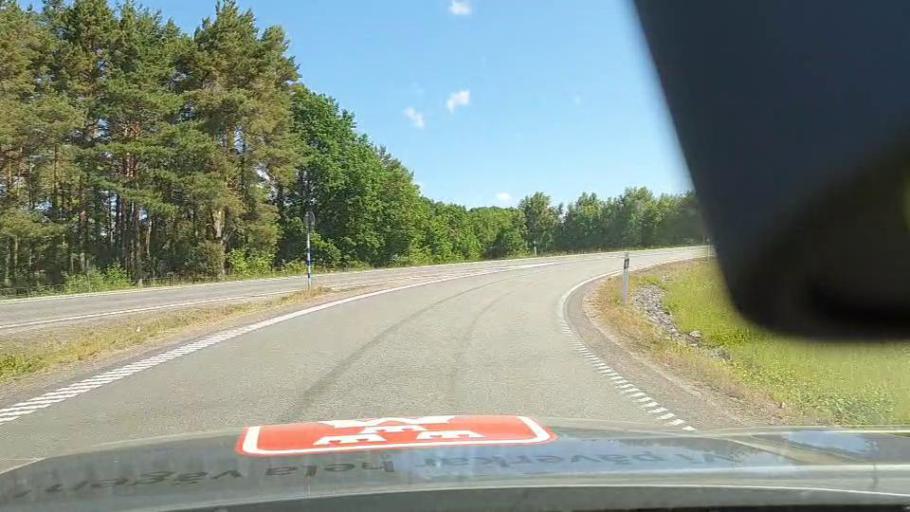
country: SE
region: Blekinge
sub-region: Solvesborgs Kommun
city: Soelvesborg
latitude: 56.0658
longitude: 14.5628
